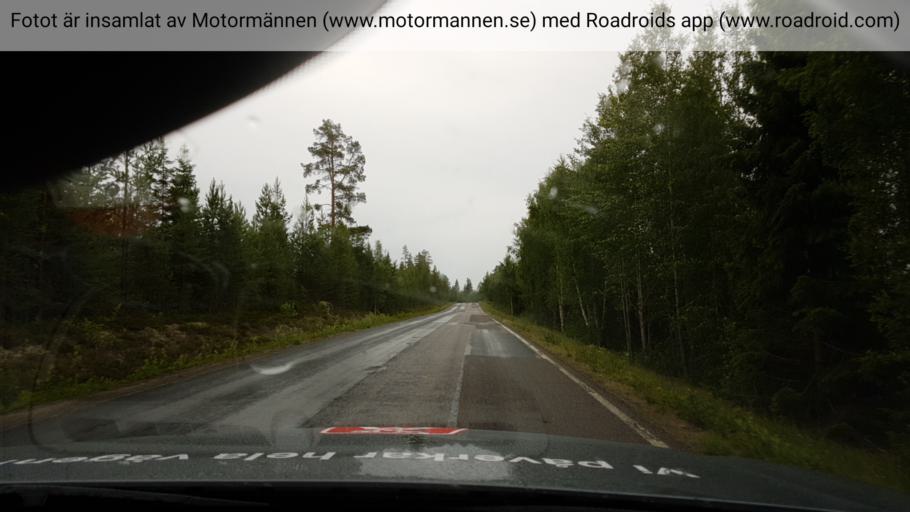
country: SE
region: Jaemtland
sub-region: Braecke Kommun
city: Braecke
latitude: 62.3073
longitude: 15.1248
